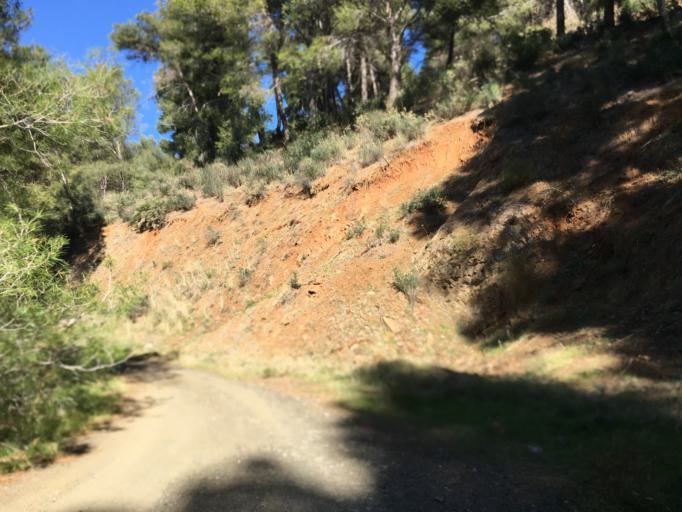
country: ES
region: Andalusia
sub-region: Provincia de Malaga
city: Malaga
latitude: 36.8037
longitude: -4.4032
